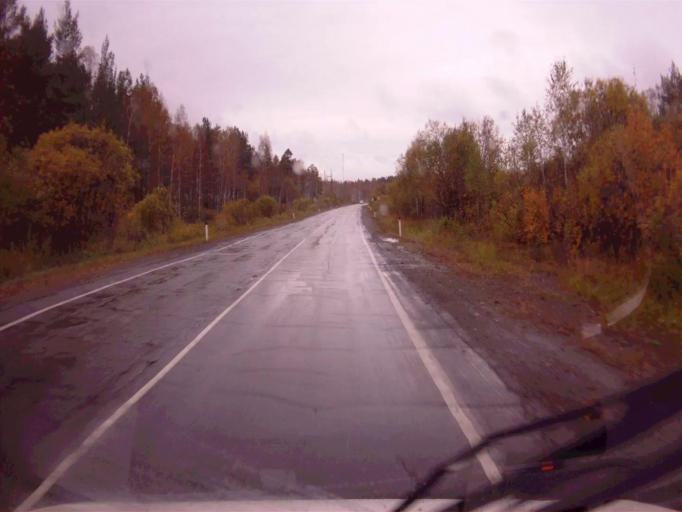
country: RU
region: Chelyabinsk
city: Verkhniy Ufaley
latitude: 55.9899
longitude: 60.3345
